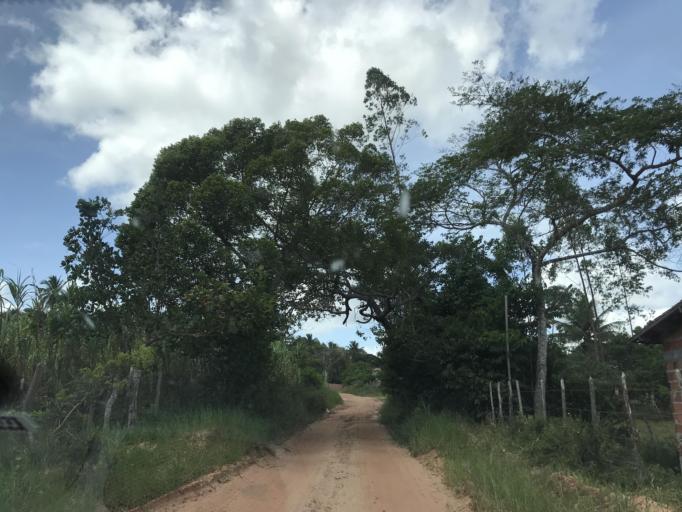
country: BR
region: Bahia
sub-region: Entre Rios
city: Entre Rios
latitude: -12.2390
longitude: -38.0975
